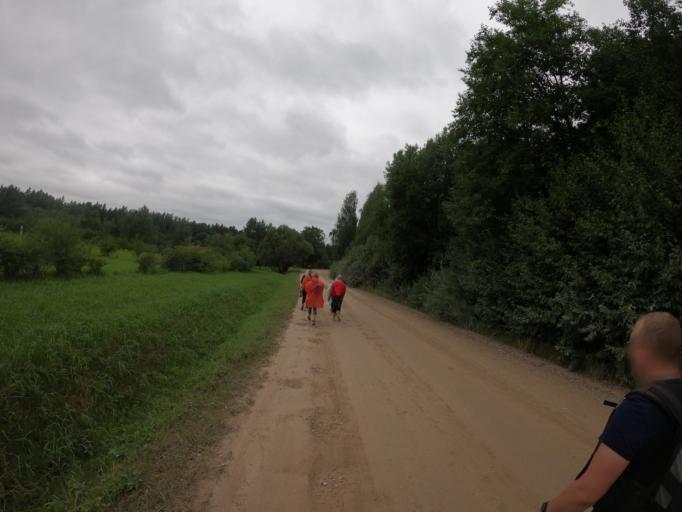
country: LV
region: Kuldigas Rajons
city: Kuldiga
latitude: 57.0051
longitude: 21.9788
